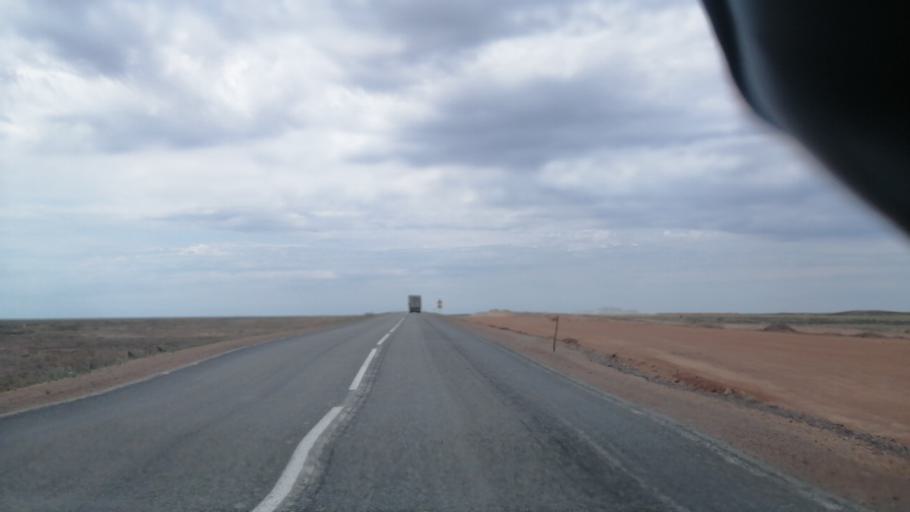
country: KZ
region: Qaraghandy
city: Saryshaghan
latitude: 46.4545
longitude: 74.0022
